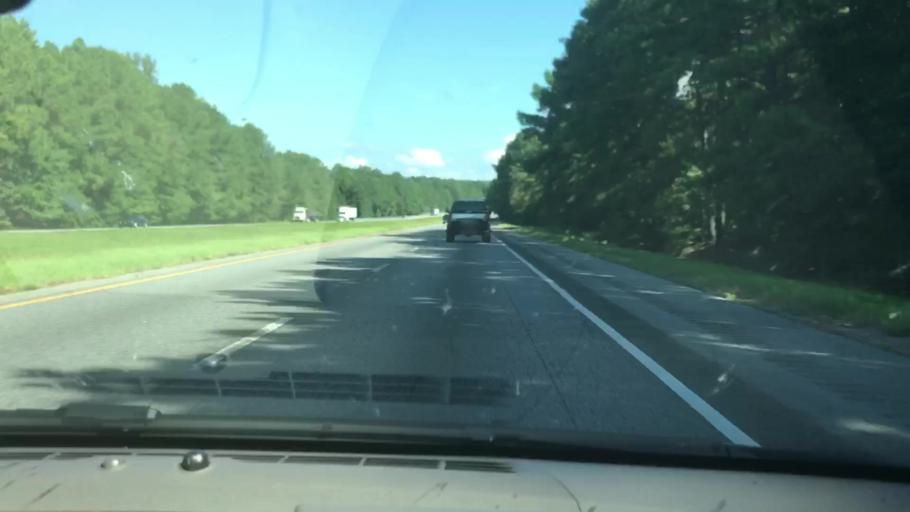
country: US
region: Alabama
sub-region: Russell County
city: Phenix City
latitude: 32.5752
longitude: -84.9615
